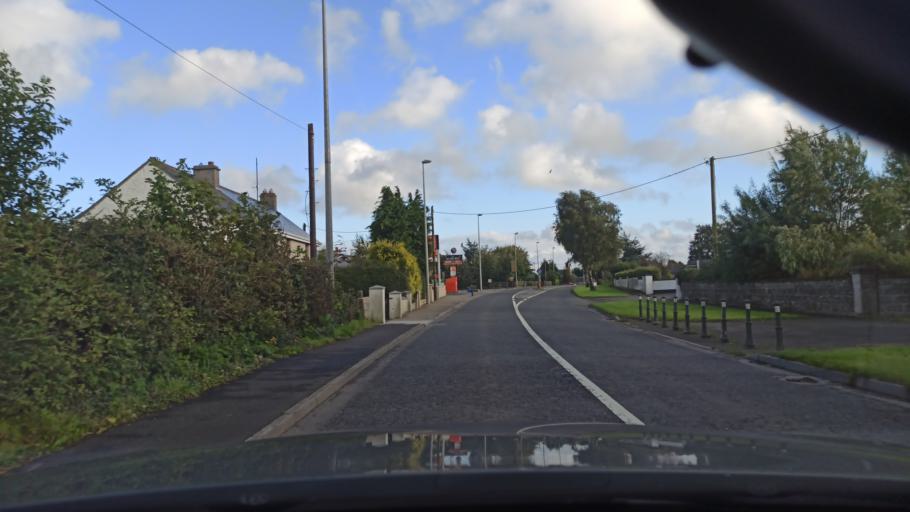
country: IE
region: Munster
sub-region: North Tipperary
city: Roscrea
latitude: 52.9407
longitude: -7.7887
